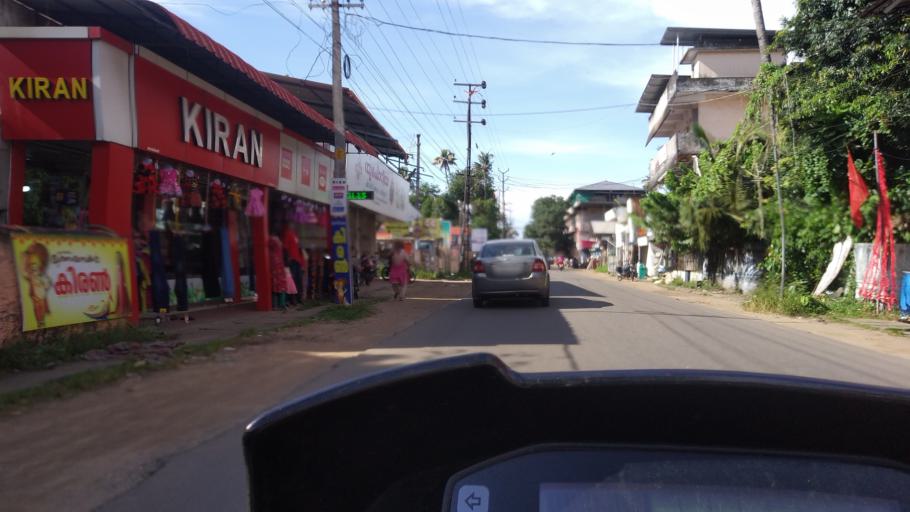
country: IN
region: Kerala
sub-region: Ernakulam
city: Elur
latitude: 10.0444
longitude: 76.2180
